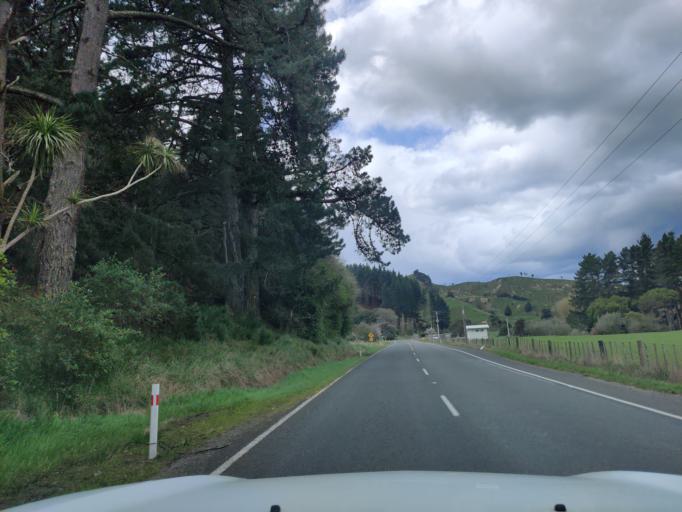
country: NZ
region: Manawatu-Wanganui
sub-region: Wanganui District
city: Wanganui
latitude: -39.8489
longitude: 175.1245
